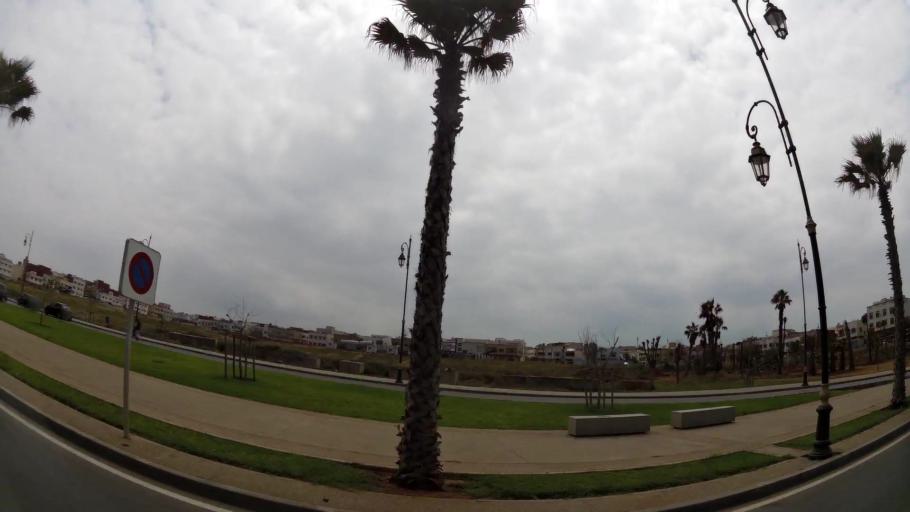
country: MA
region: Rabat-Sale-Zemmour-Zaer
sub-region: Skhirate-Temara
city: Temara
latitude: 33.9808
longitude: -6.8956
